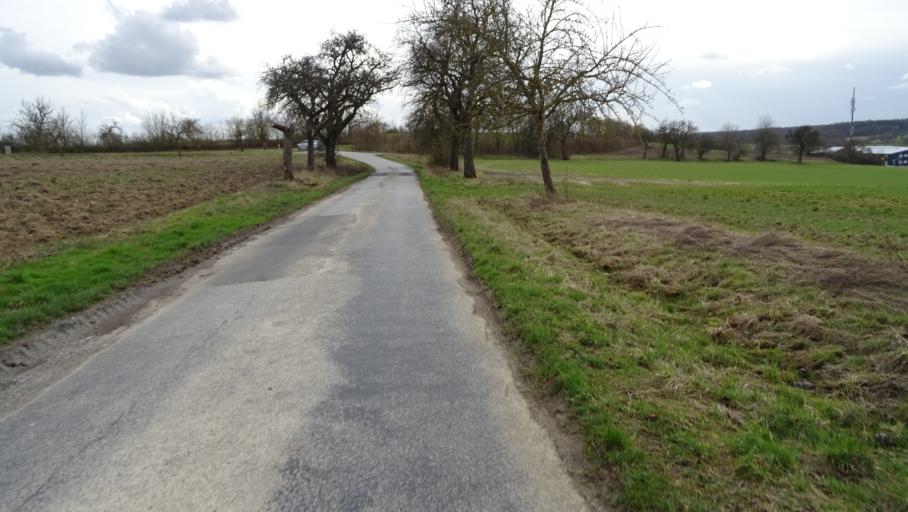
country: DE
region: Baden-Wuerttemberg
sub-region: Karlsruhe Region
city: Limbach
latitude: 49.4271
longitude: 9.2466
